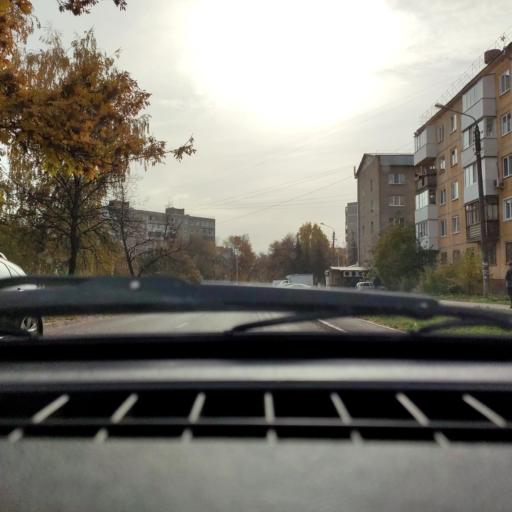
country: RU
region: Bashkortostan
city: Ufa
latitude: 54.8126
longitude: 56.1196
